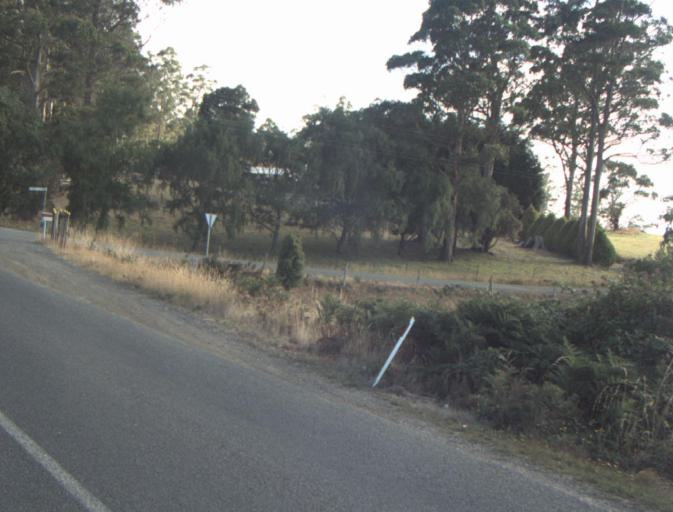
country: AU
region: Tasmania
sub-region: Launceston
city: Mayfield
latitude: -41.2076
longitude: 147.2151
